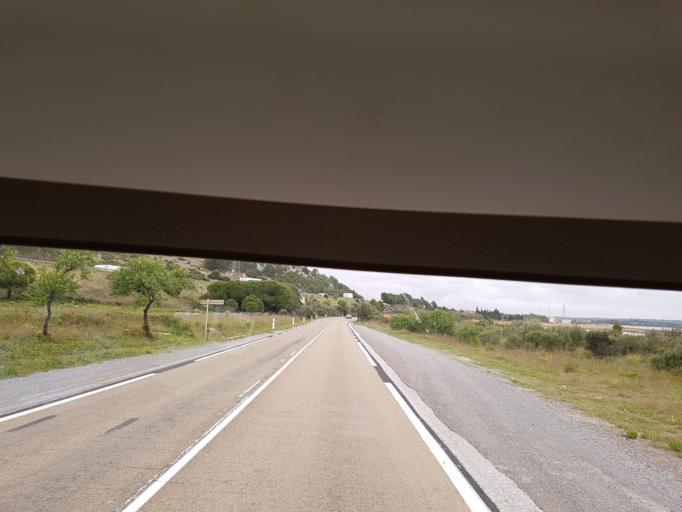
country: FR
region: Languedoc-Roussillon
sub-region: Departement de l'Aude
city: Leucate
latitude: 42.8808
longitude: 2.9931
